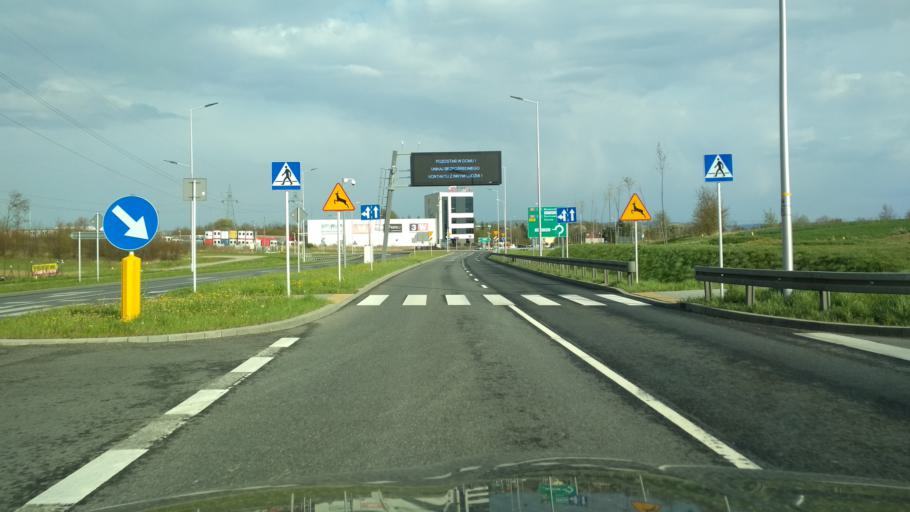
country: PL
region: Subcarpathian Voivodeship
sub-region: Powiat rzeszowski
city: Kielanowka
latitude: 50.0148
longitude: 21.9567
